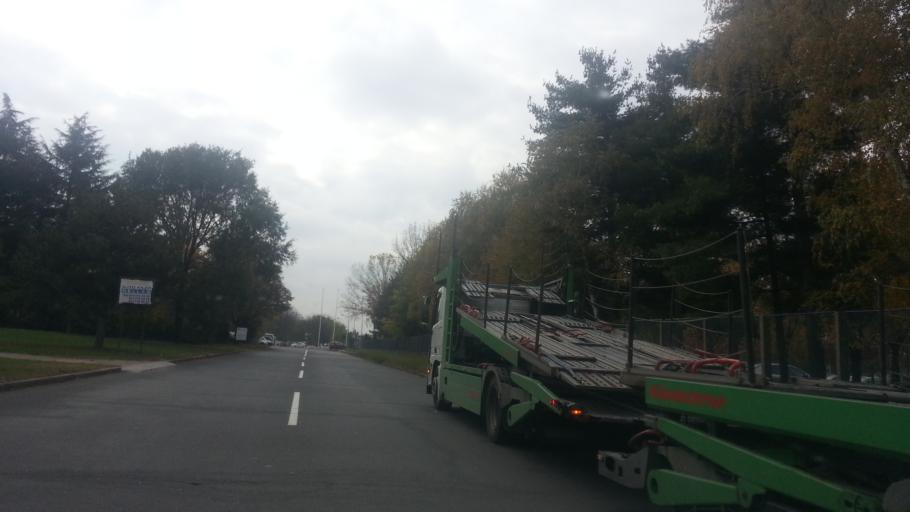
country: RS
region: Central Serbia
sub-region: Belgrade
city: Zemun
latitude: 44.8604
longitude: 20.3664
